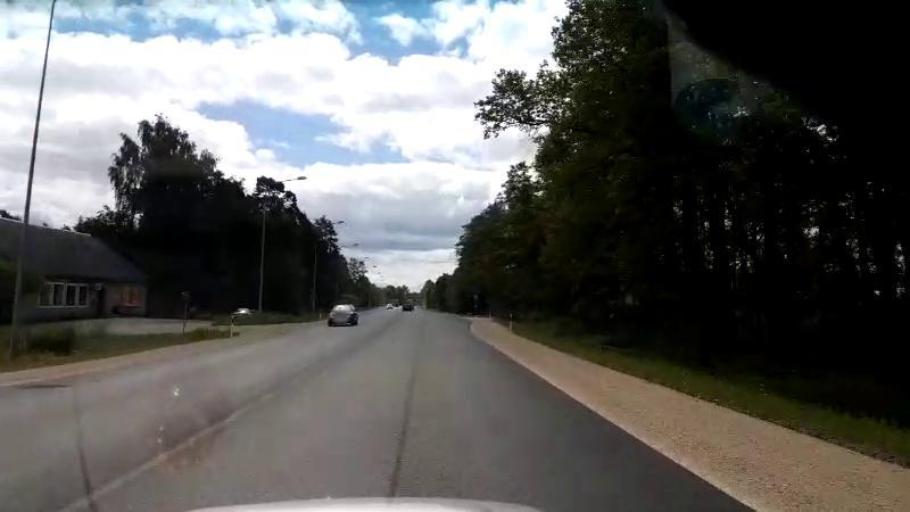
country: LV
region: Salacgrivas
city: Salacgriva
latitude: 57.7904
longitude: 24.3532
